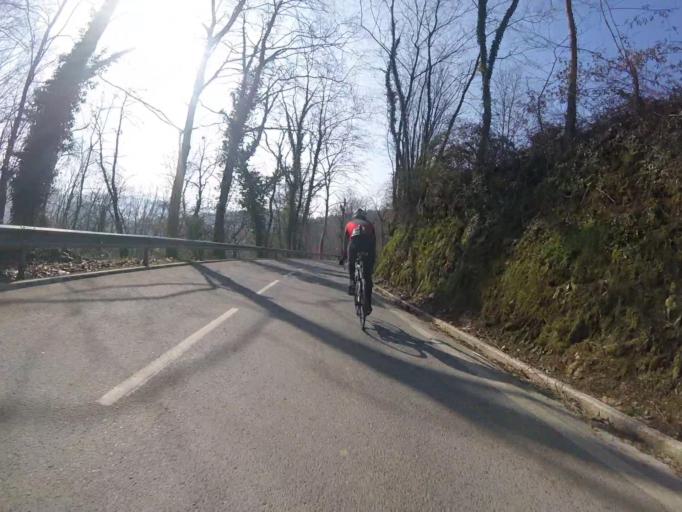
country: ES
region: Navarre
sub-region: Provincia de Navarra
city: Bera
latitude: 43.2965
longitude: -1.6899
